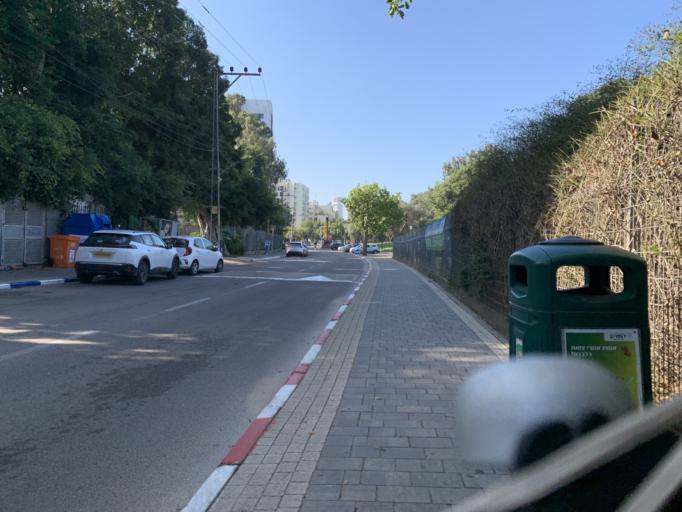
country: IL
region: Tel Aviv
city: Ramat Gan
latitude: 32.0965
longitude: 34.8158
